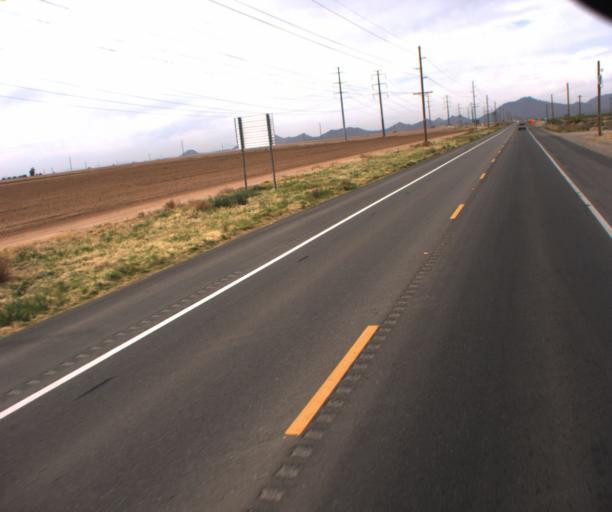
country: US
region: Arizona
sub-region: Pinal County
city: Coolidge
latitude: 33.0025
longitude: -111.5458
